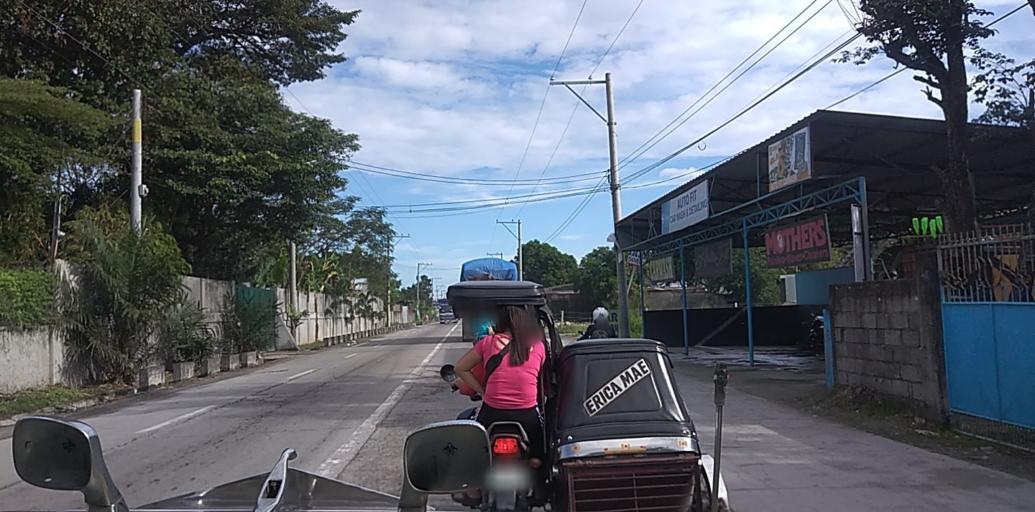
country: PH
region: Central Luzon
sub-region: Province of Pampanga
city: Bulaon
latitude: 15.0985
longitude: 120.6570
